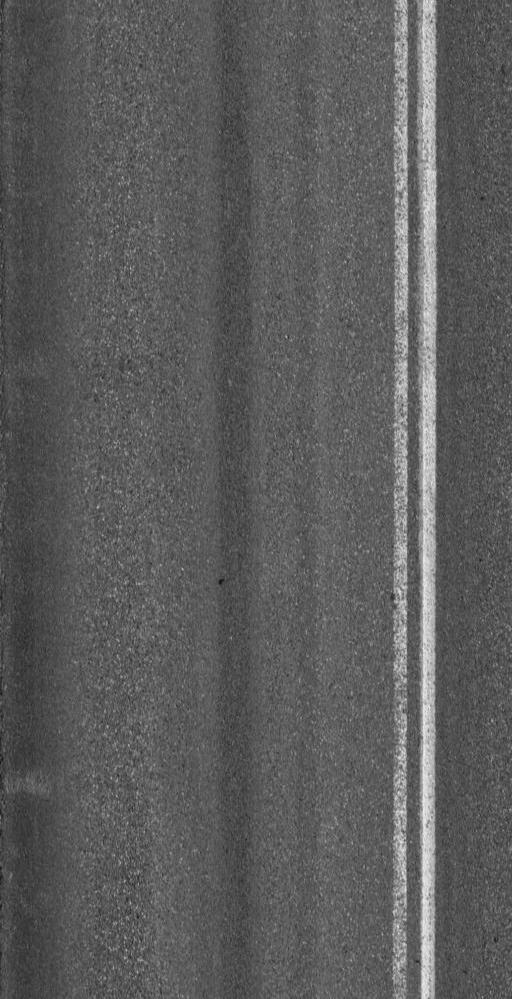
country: US
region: Vermont
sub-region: Chittenden County
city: Milton
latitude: 44.6067
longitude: -73.1242
